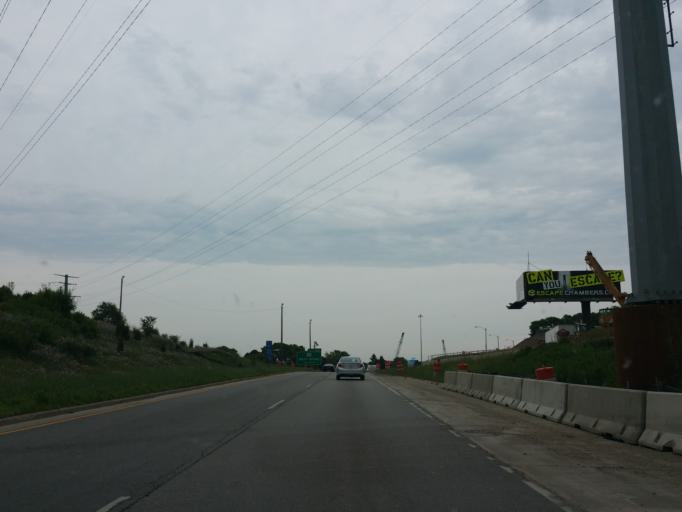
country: US
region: Wisconsin
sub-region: Milwaukee County
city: West Allis
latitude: 43.0269
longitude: -88.0334
